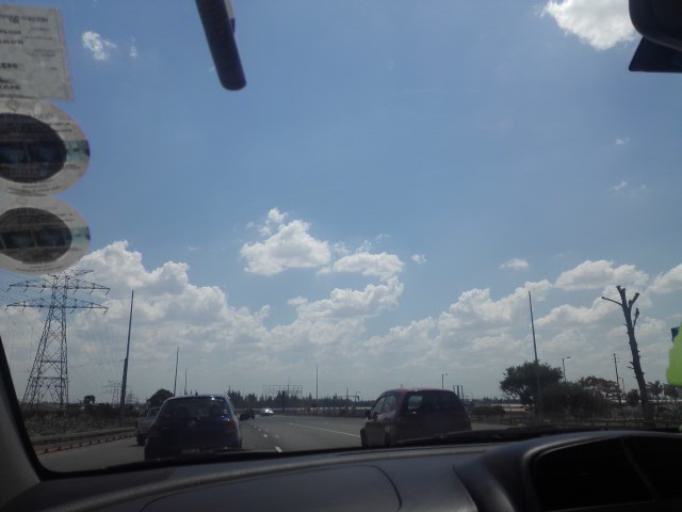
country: MZ
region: Maputo
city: Matola
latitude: -25.9363
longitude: 32.4953
